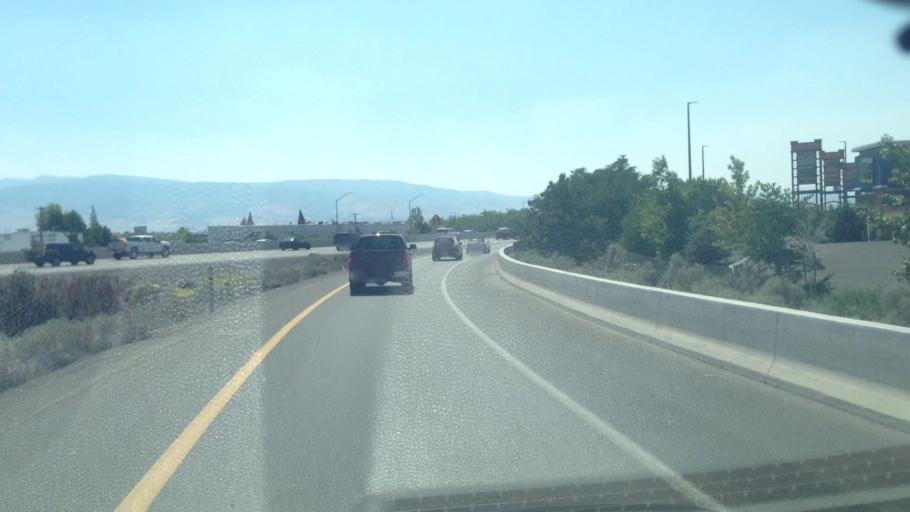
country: US
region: Nevada
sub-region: Washoe County
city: Sparks
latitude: 39.5291
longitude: -119.7183
